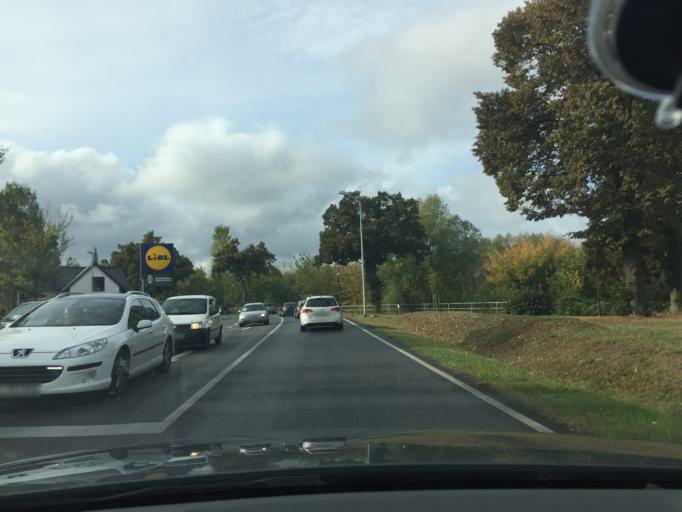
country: DE
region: Berlin
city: Hellersdorf
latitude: 52.5411
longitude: 13.6385
